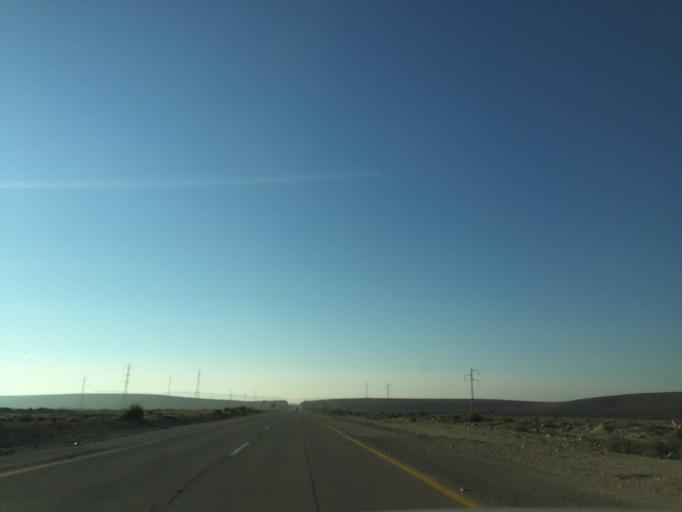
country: IL
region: Southern District
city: Mitzpe Ramon
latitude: 30.4678
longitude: 34.9334
